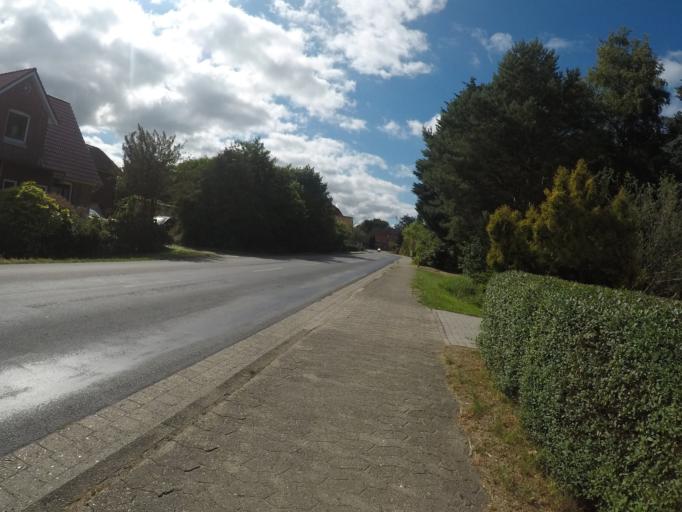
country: DE
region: Lower Saxony
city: Osterbruch
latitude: 53.7771
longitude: 8.9444
